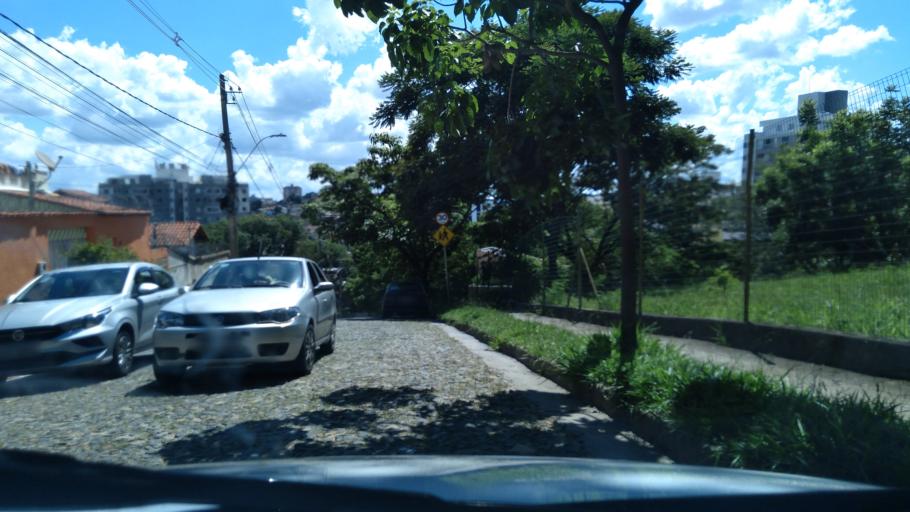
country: BR
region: Minas Gerais
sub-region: Belo Horizonte
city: Belo Horizonte
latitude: -19.8735
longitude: -43.9133
